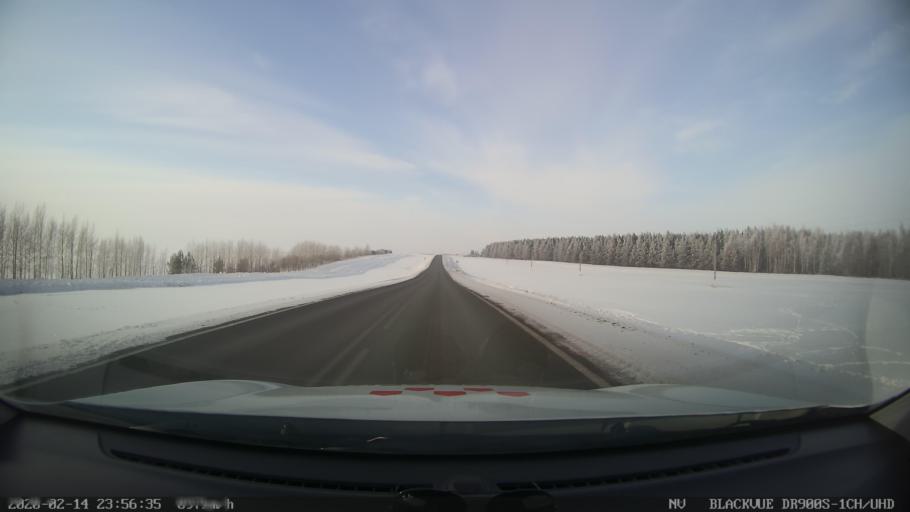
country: RU
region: Tatarstan
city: Kuybyshevskiy Zaton
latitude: 55.3263
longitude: 49.1273
